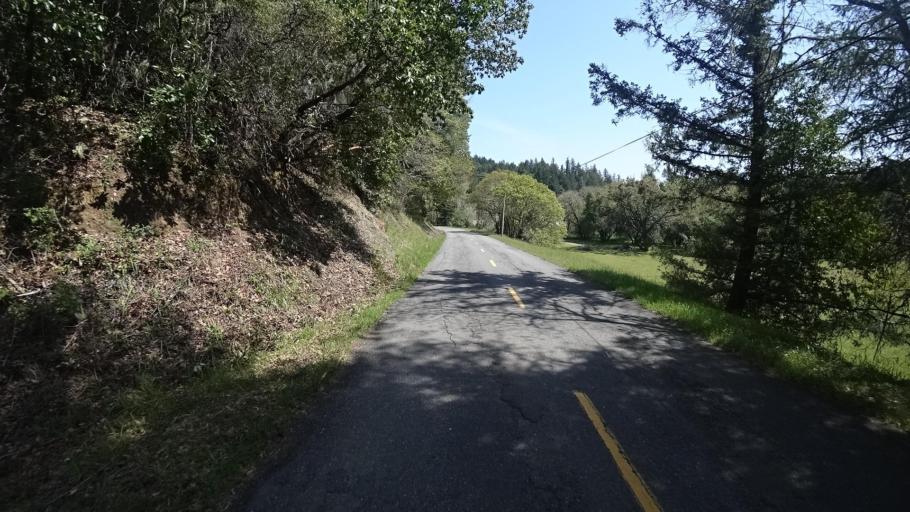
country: US
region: California
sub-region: Humboldt County
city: Redway
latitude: 40.3104
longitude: -123.6572
